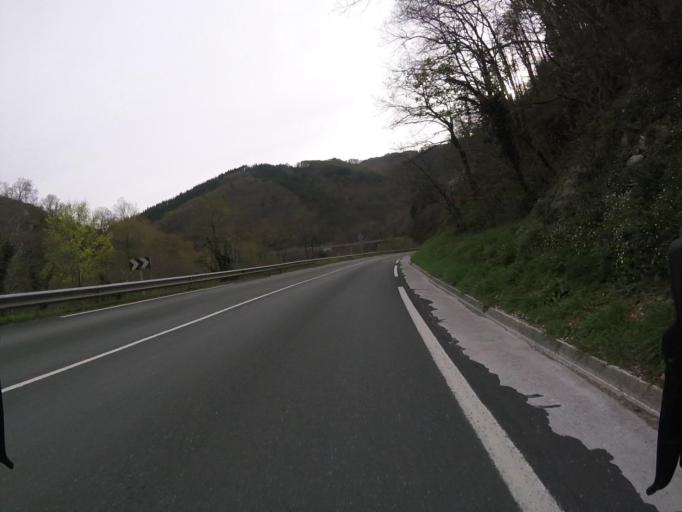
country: ES
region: Basque Country
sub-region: Provincia de Guipuzcoa
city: Irun
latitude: 43.3134
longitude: -1.7390
